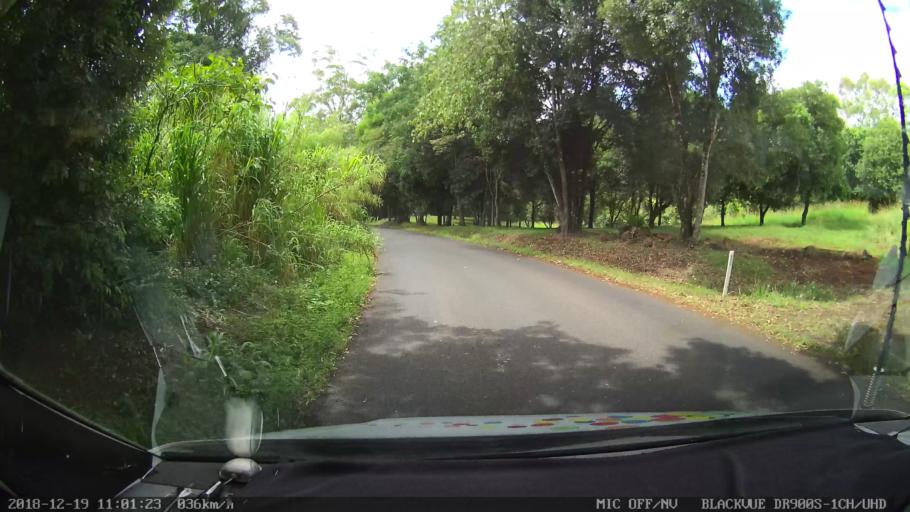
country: AU
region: New South Wales
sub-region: Lismore Municipality
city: Nimbin
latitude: -28.6037
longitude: 153.2663
